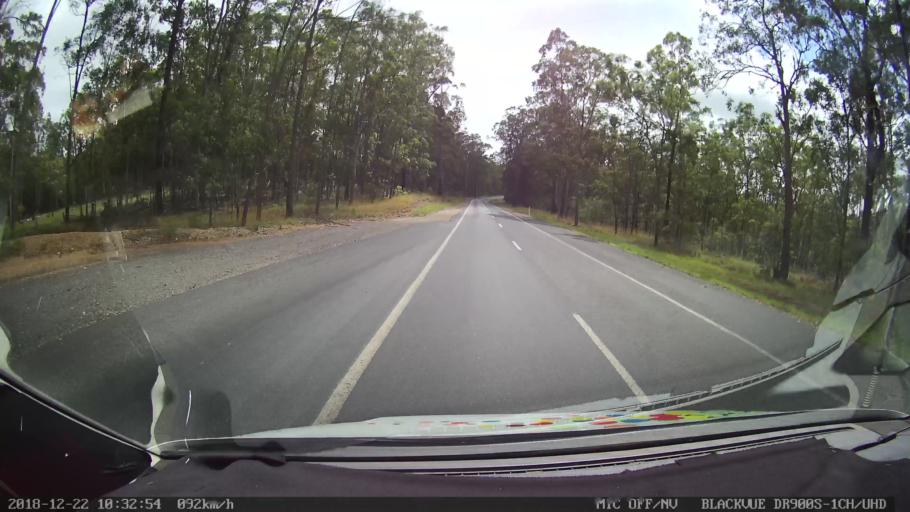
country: AU
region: New South Wales
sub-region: Clarence Valley
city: South Grafton
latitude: -29.6178
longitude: 152.6467
